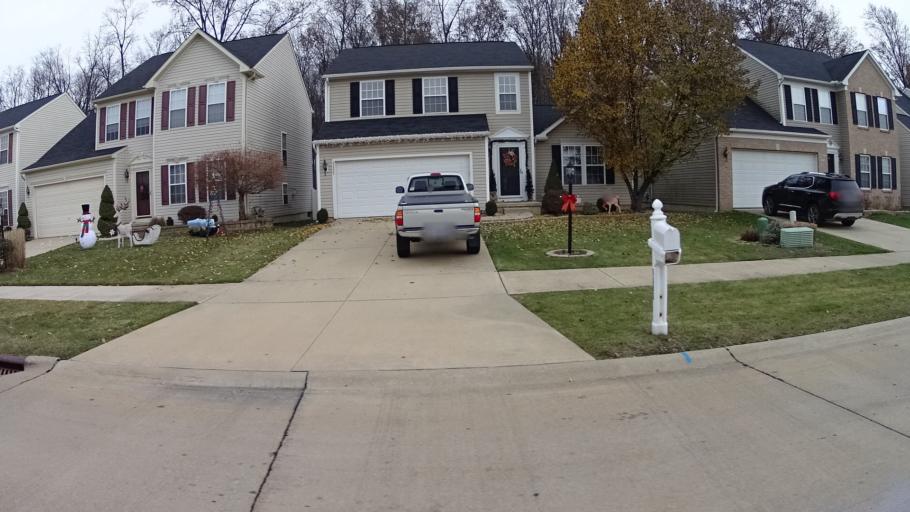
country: US
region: Ohio
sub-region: Lorain County
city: North Ridgeville
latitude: 41.4123
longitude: -82.0484
